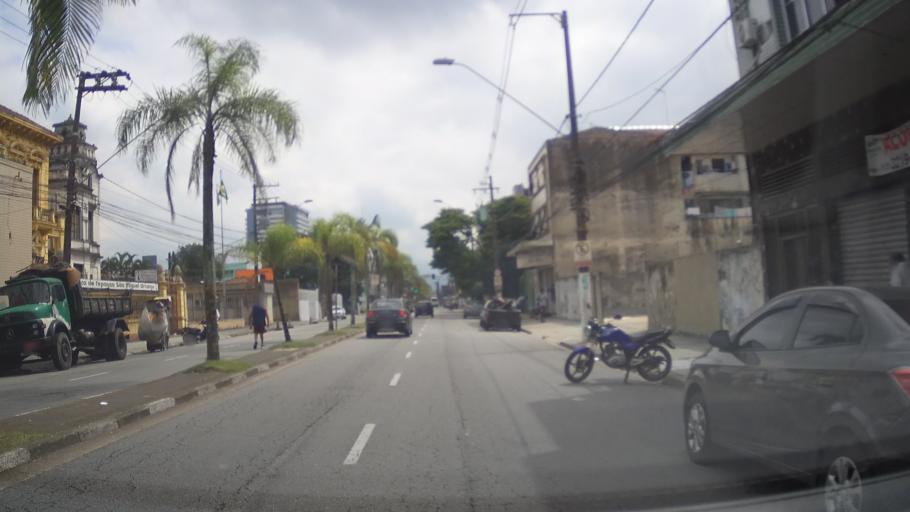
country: BR
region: Sao Paulo
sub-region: Santos
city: Santos
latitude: -23.9418
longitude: -46.3213
